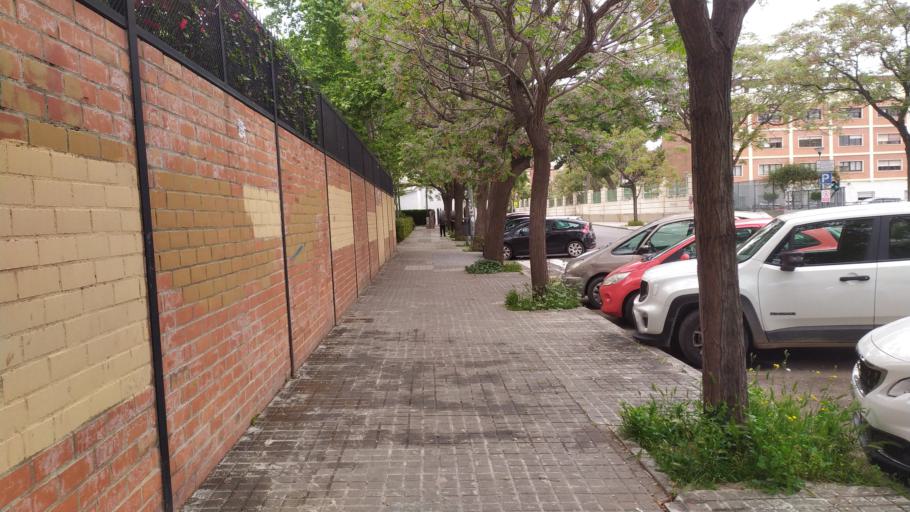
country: ES
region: Valencia
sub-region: Provincia de Valencia
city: Mislata
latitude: 39.4679
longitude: -0.4103
